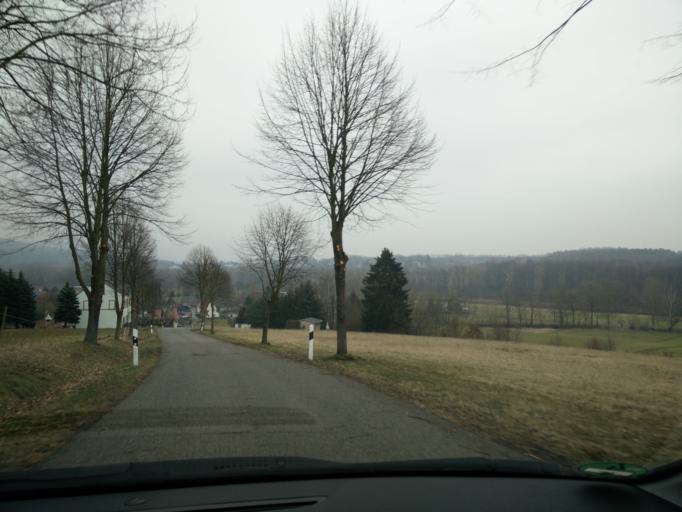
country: DE
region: Saxony
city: Wechselburg
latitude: 50.9914
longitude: 12.7696
